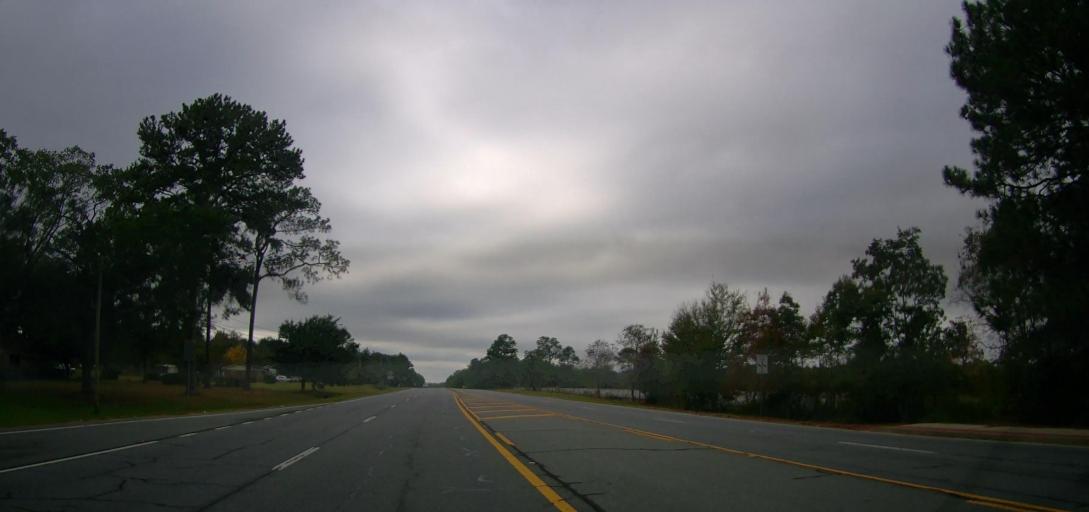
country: US
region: Georgia
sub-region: Colquitt County
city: Moultrie
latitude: 31.2620
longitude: -83.6952
